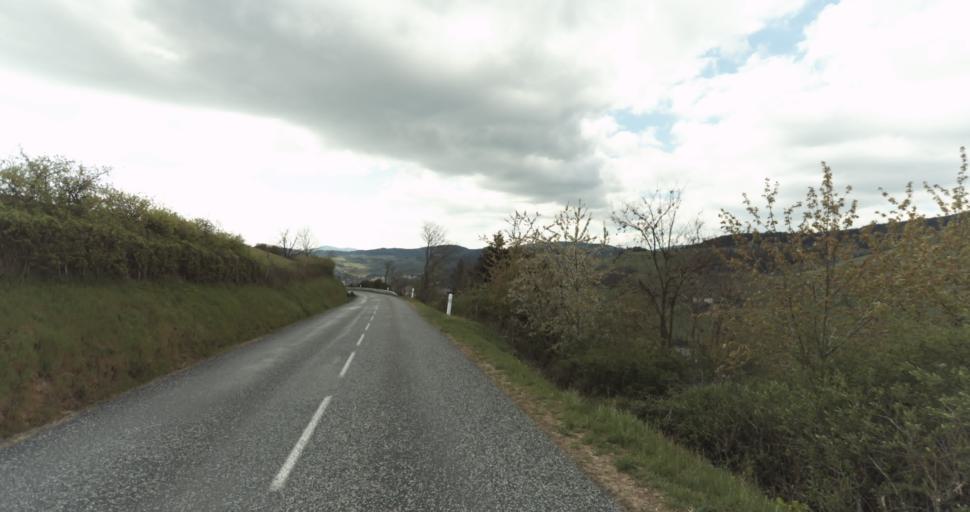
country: FR
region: Rhone-Alpes
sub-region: Departement du Rhone
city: Tarare
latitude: 45.9135
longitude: 4.4286
